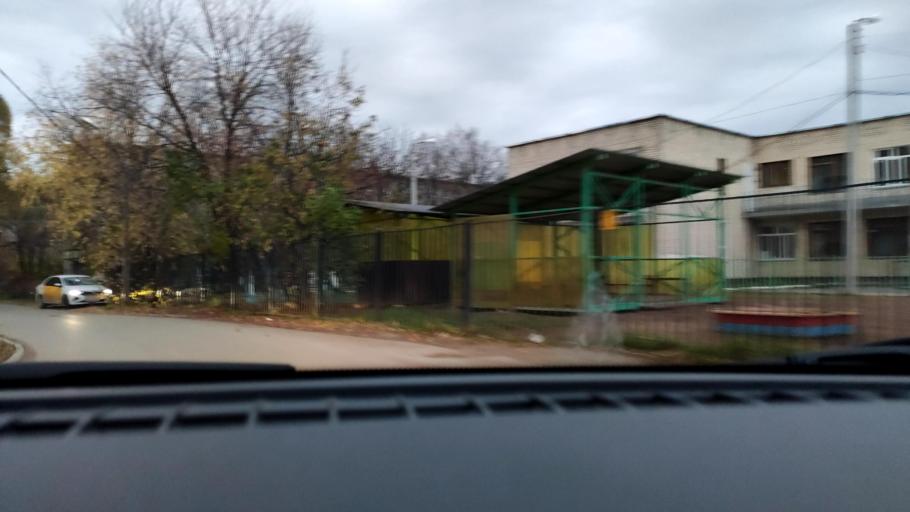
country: RU
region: Perm
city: Perm
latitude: 57.9628
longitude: 56.2245
